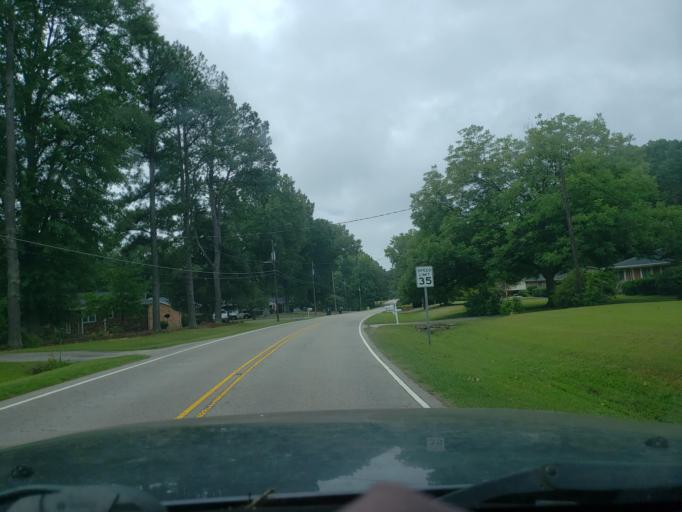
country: US
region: North Carolina
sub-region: Durham County
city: Gorman
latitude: 35.9737
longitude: -78.7847
